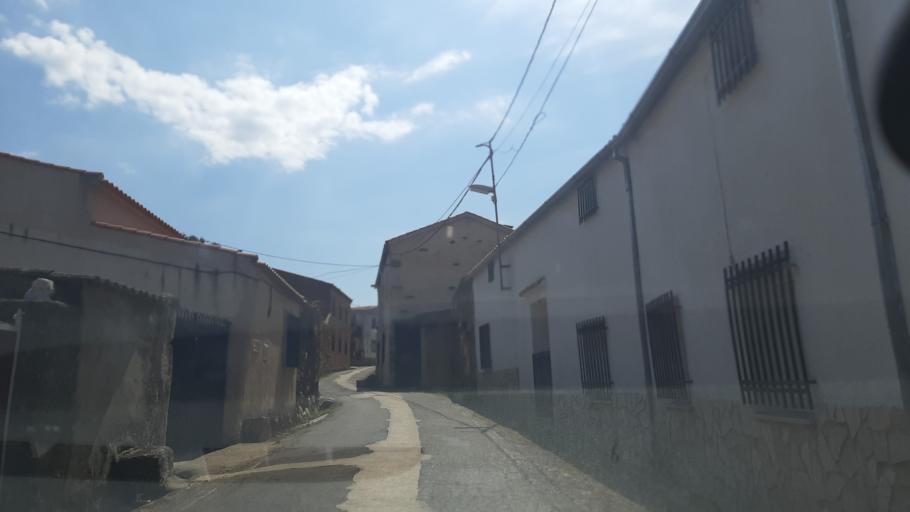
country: ES
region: Castille and Leon
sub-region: Provincia de Salamanca
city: Gallegos de Arganan
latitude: 40.6512
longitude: -6.7601
